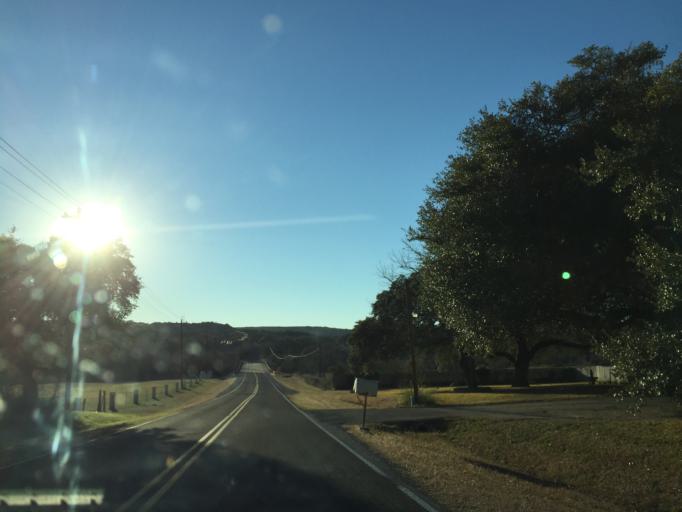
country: US
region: Texas
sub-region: Travis County
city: Lago Vista
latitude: 30.5091
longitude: -98.0403
